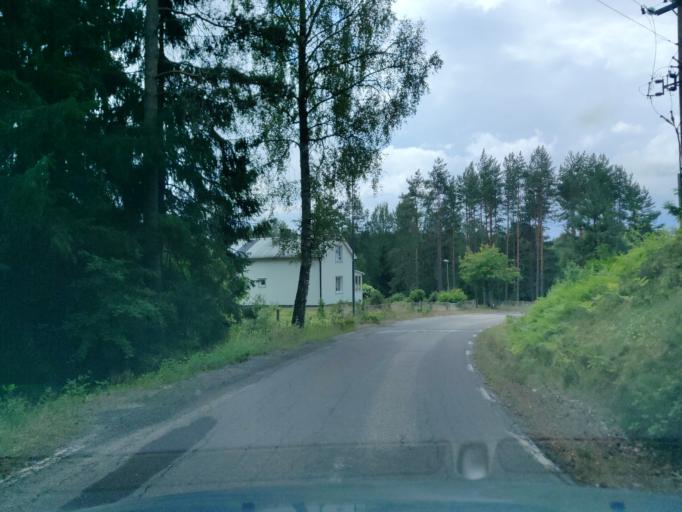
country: SE
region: Vaermland
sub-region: Munkfors Kommun
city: Munkfors
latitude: 59.9228
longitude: 13.5710
